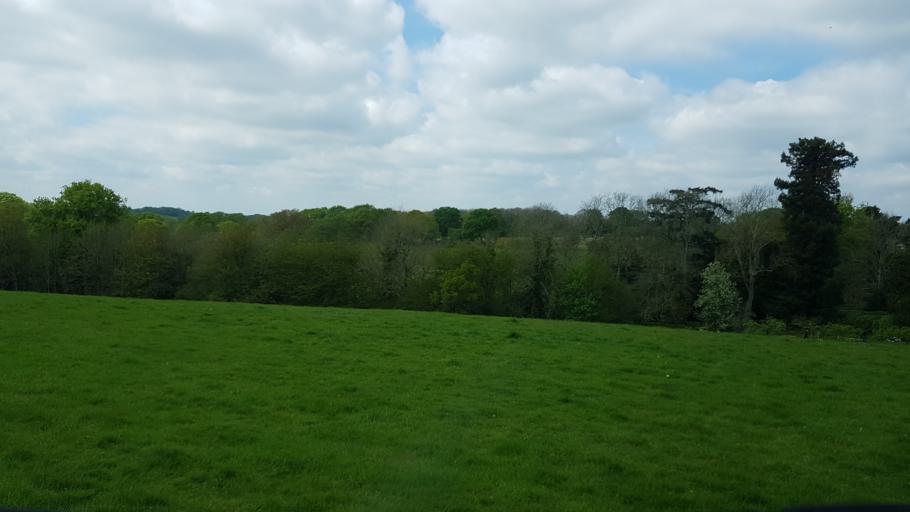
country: GB
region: England
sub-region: East Sussex
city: Robertsbridge
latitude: 51.0341
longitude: 0.4343
